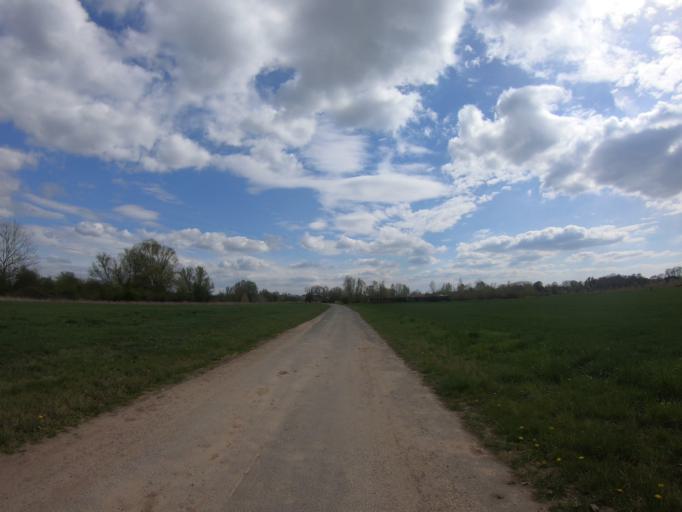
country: DE
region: Lower Saxony
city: Sarstedt
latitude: 52.2527
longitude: 9.8283
